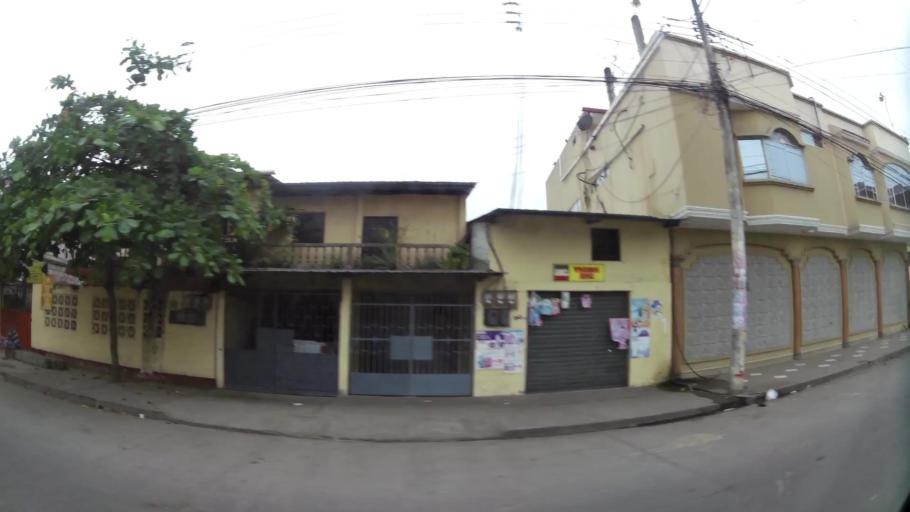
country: EC
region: El Oro
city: Puerto Bolivar
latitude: -3.2684
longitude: -79.9986
